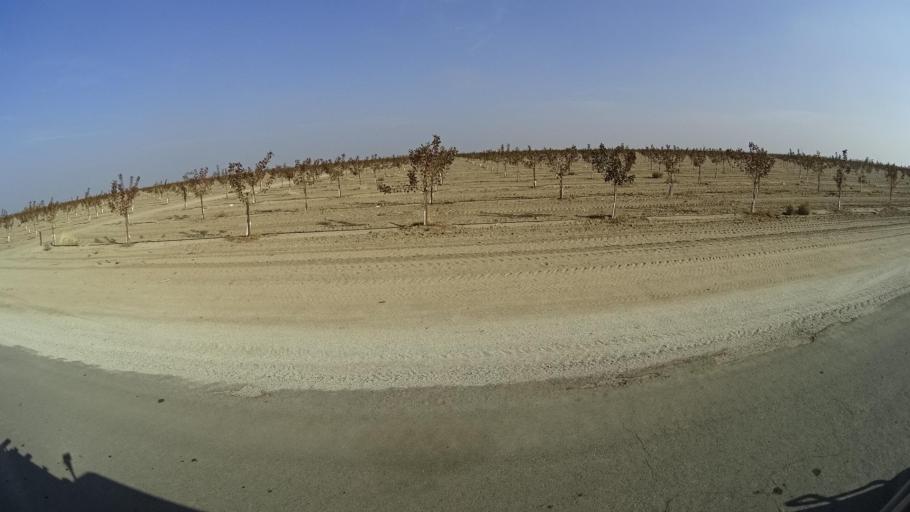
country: US
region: California
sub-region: Tulare County
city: Richgrove
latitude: 35.7834
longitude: -119.1163
